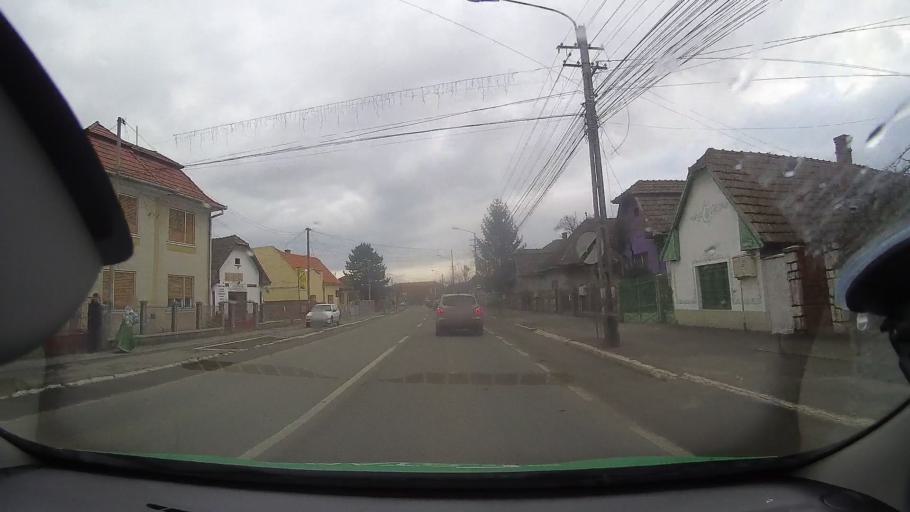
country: RO
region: Cluj
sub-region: Municipiul Campia Turzii
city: Campia Turzii
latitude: 46.5510
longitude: 23.8855
